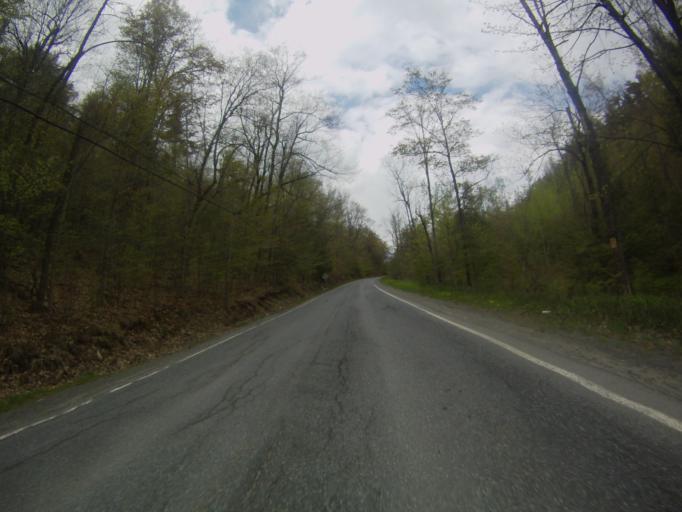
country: US
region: New York
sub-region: Essex County
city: Port Henry
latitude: 43.9826
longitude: -73.4896
